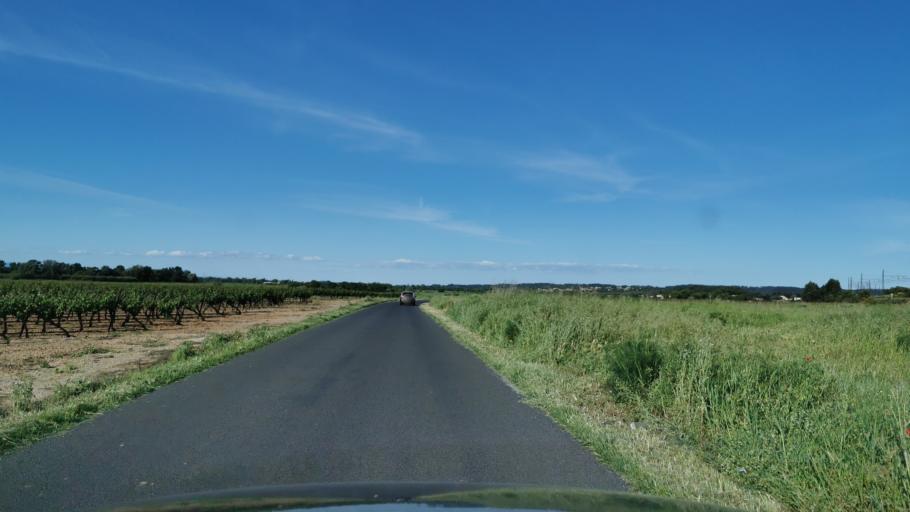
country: FR
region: Languedoc-Roussillon
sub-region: Departement de l'Aude
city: Nevian
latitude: 43.2131
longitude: 2.8808
